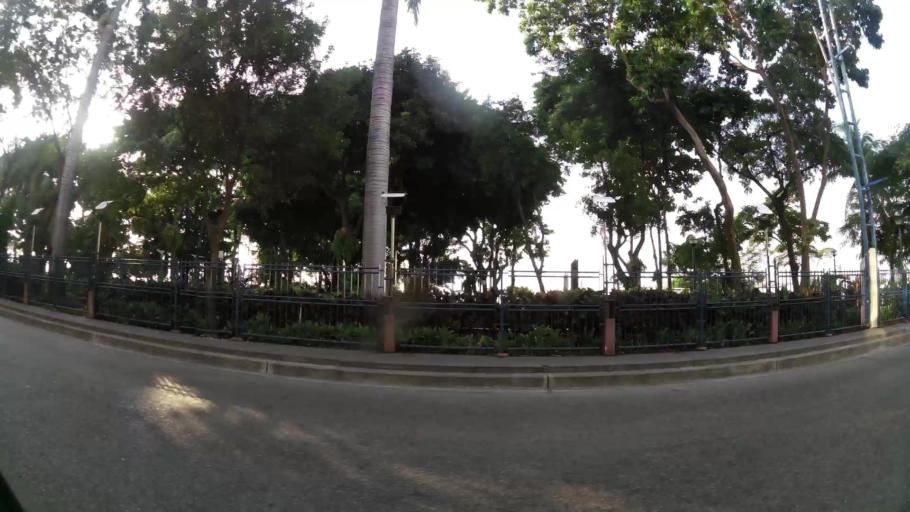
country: EC
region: Guayas
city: Eloy Alfaro
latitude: -2.1886
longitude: -79.8783
